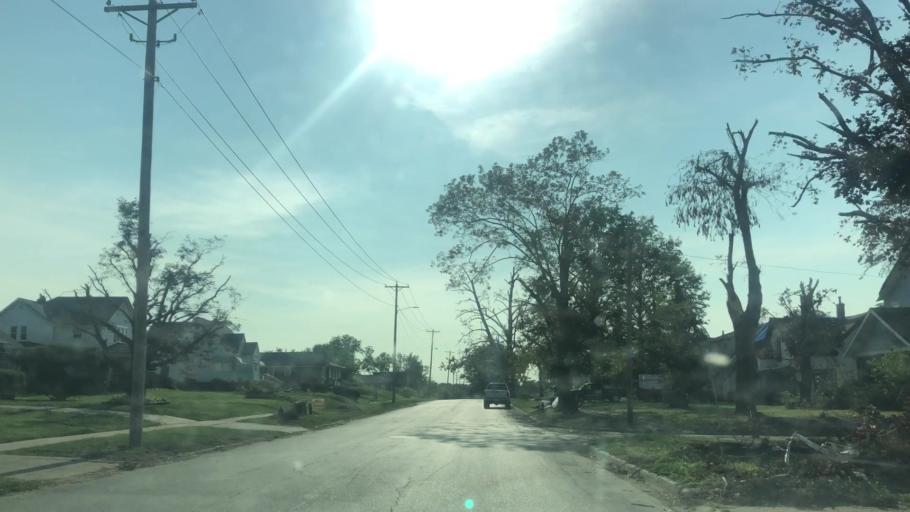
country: US
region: Iowa
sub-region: Marshall County
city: Marshalltown
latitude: 42.0527
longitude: -92.9421
